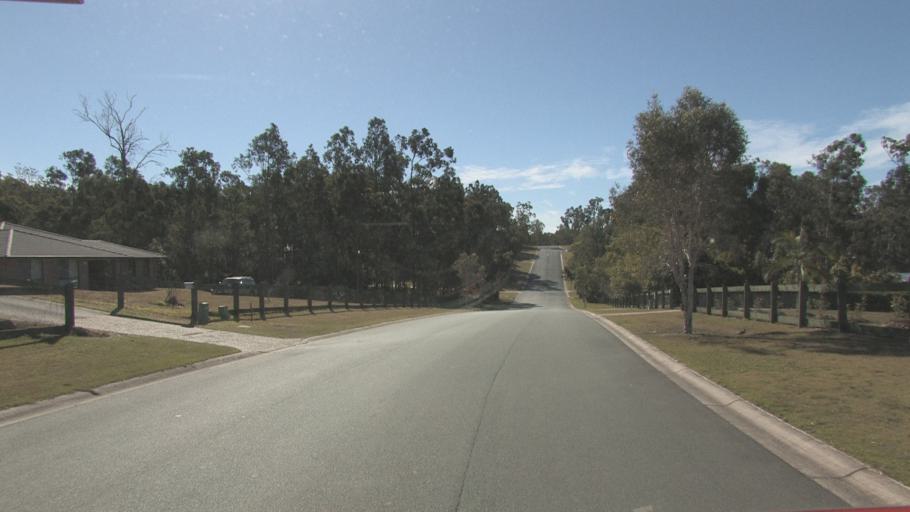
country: AU
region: Queensland
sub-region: Ipswich
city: Springfield Lakes
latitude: -27.7394
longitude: 152.9189
